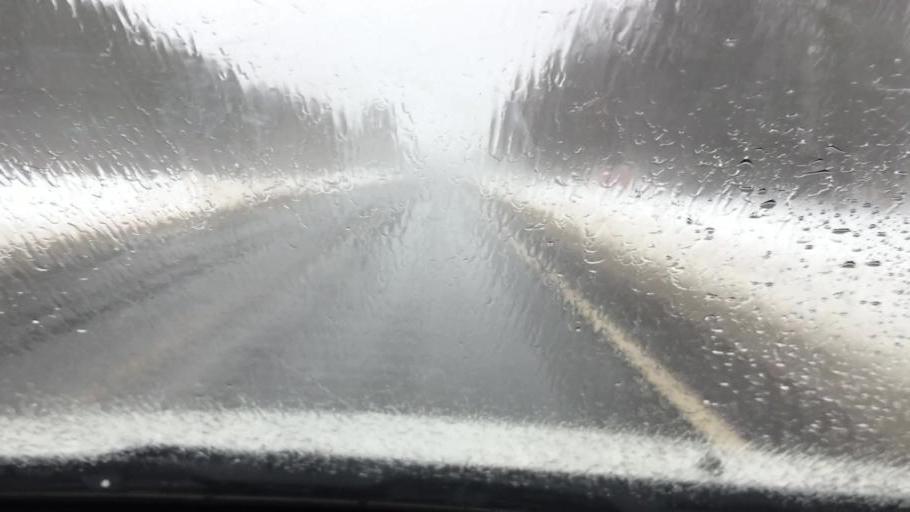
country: US
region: Michigan
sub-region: Antrim County
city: Mancelona
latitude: 44.9397
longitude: -85.0509
